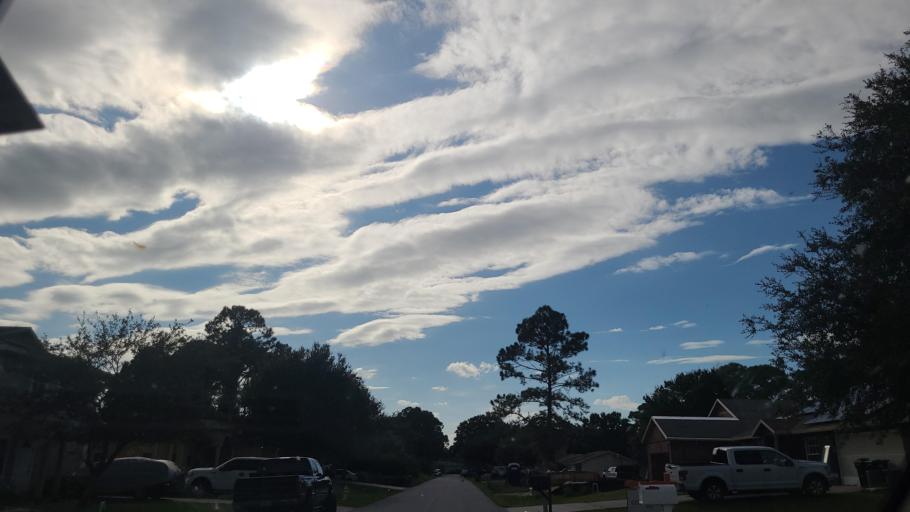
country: US
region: Florida
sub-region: Brevard County
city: Palm Bay
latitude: 27.9776
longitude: -80.6520
